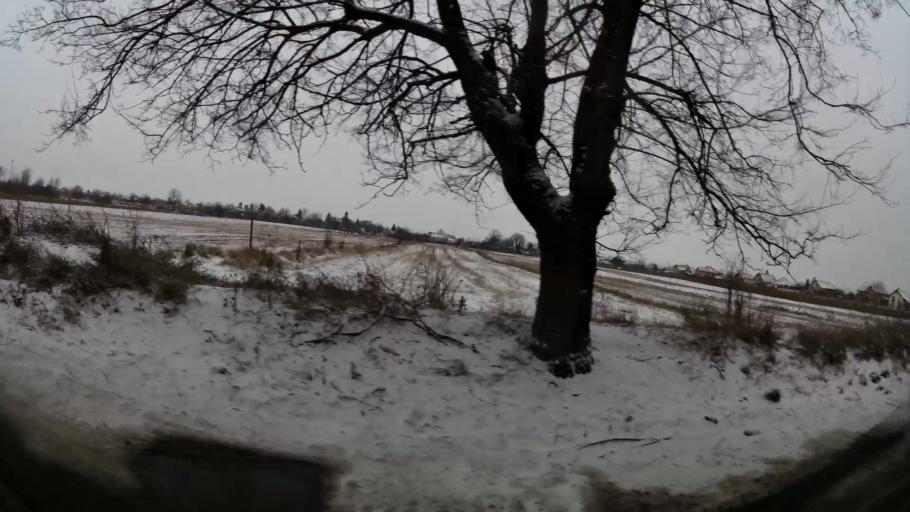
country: RO
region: Dambovita
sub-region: Comuna Ulmi
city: Ulmi
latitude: 44.8991
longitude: 25.5037
